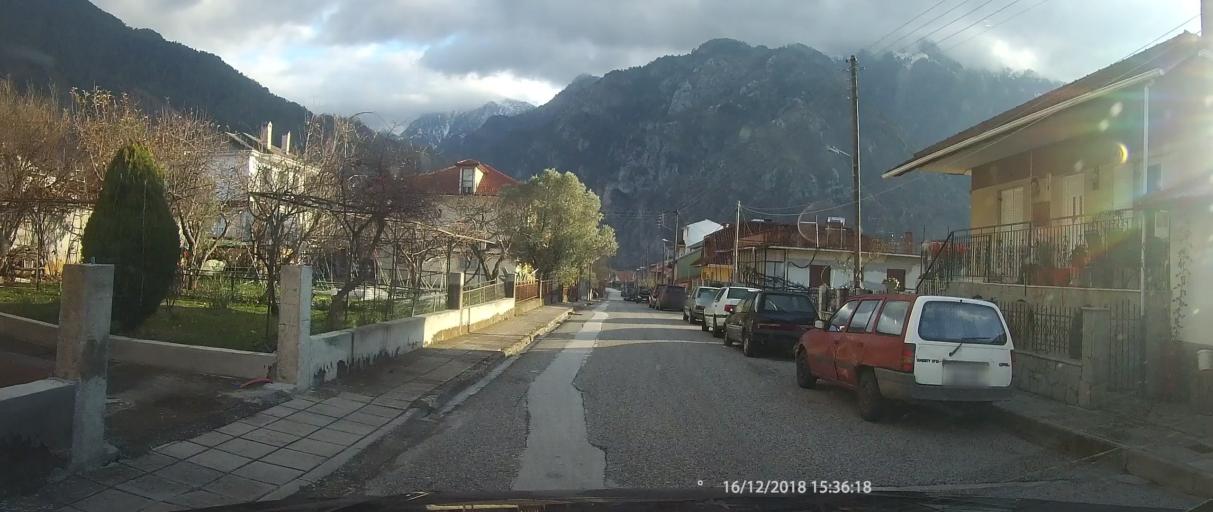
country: GR
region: Epirus
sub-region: Nomos Ioanninon
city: Konitsa
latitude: 40.0464
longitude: 20.7398
